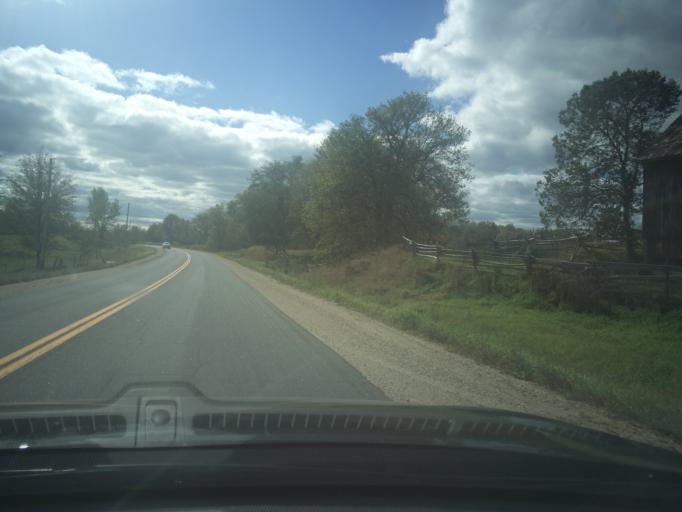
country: CA
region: Ontario
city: Perth
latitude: 44.7776
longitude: -76.3583
